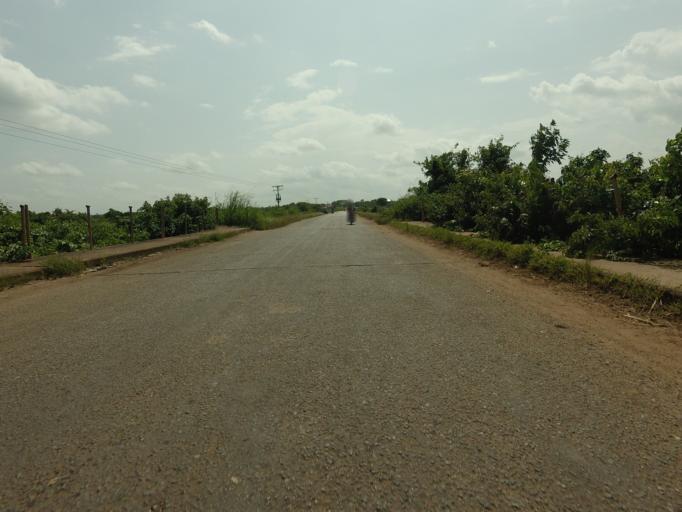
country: TG
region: Maritime
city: Lome
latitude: 6.2474
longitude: 0.9773
